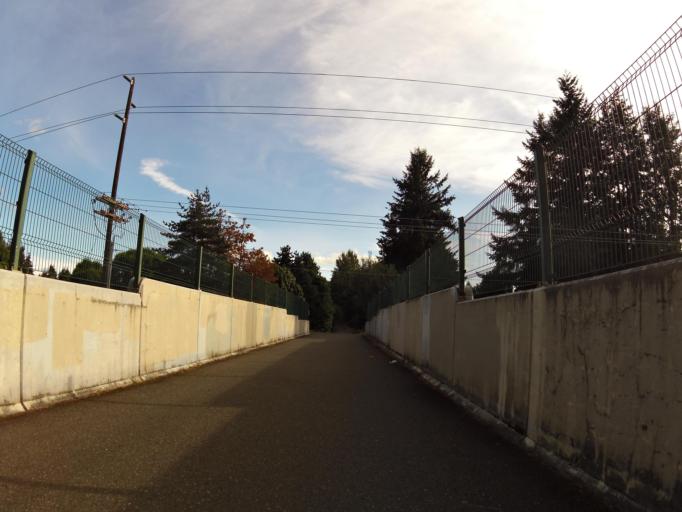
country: US
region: Washington
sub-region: Thurston County
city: Lacey
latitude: 46.9964
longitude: -122.8336
